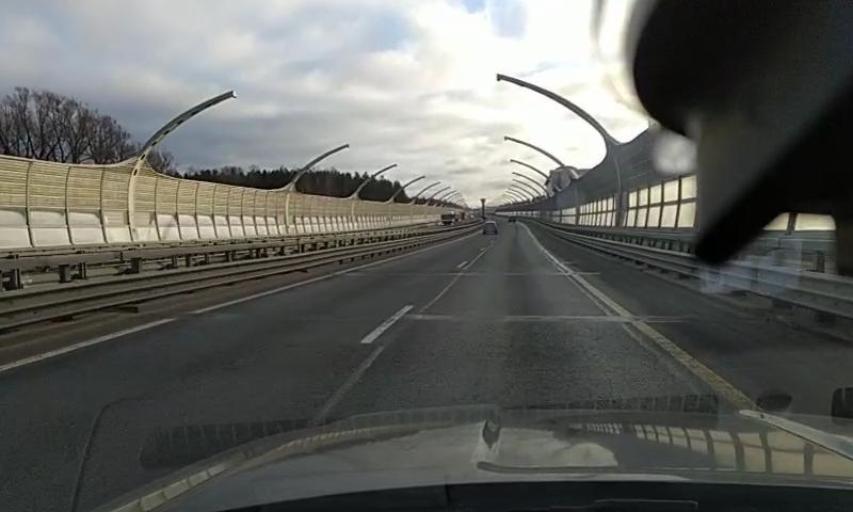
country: RU
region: St.-Petersburg
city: Beloostrov
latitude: 60.1451
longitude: 30.0136
